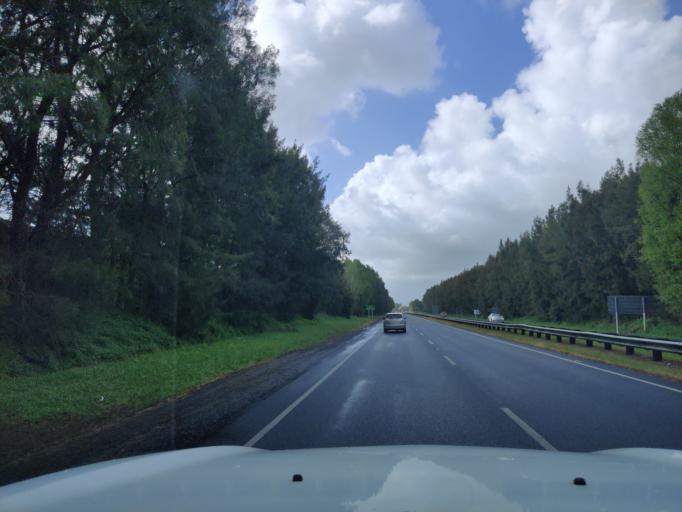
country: NZ
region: Waikato
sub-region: Hamilton City
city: Hamilton
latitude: -37.8317
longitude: 175.3609
